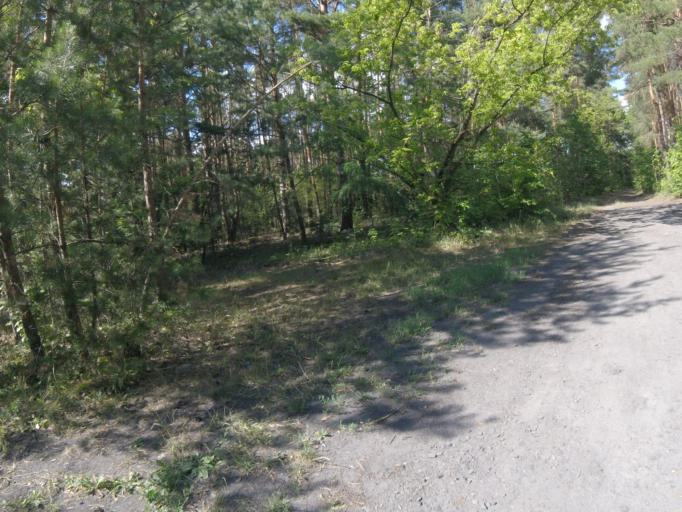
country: DE
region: Brandenburg
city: Wildau
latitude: 52.3295
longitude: 13.6604
